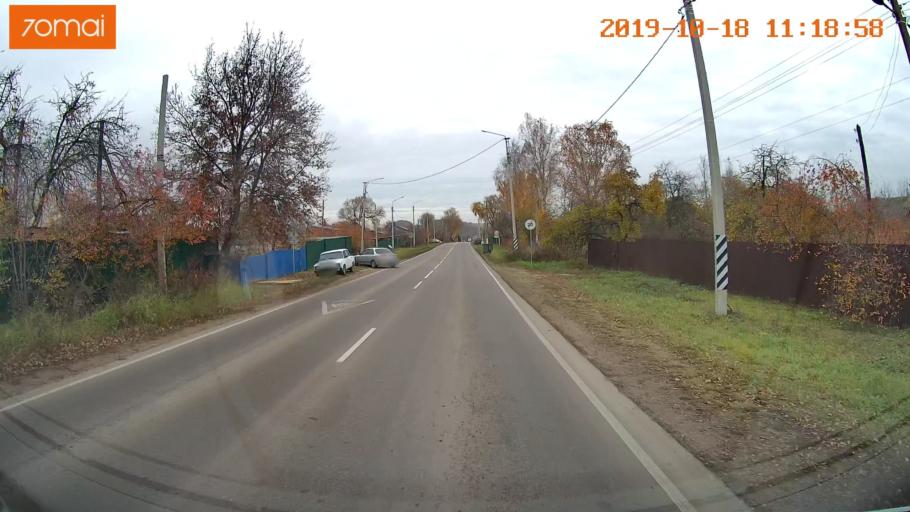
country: RU
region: Tula
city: Kimovsk
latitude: 54.0418
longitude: 38.5512
